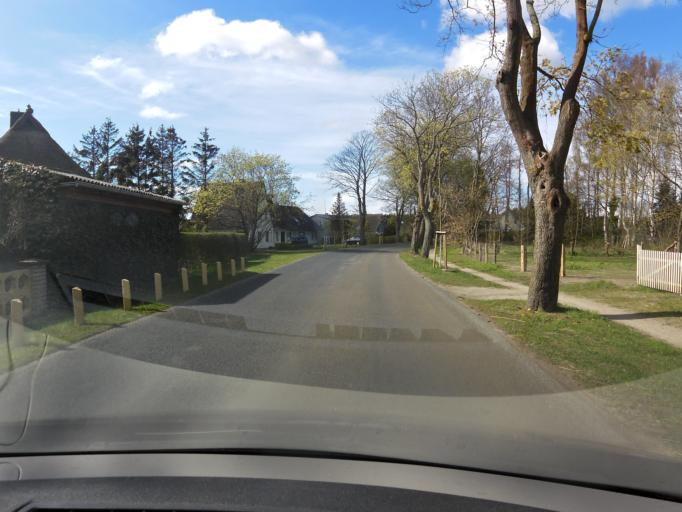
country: DE
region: Mecklenburg-Vorpommern
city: Ostseebad Prerow
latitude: 54.4128
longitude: 12.5811
